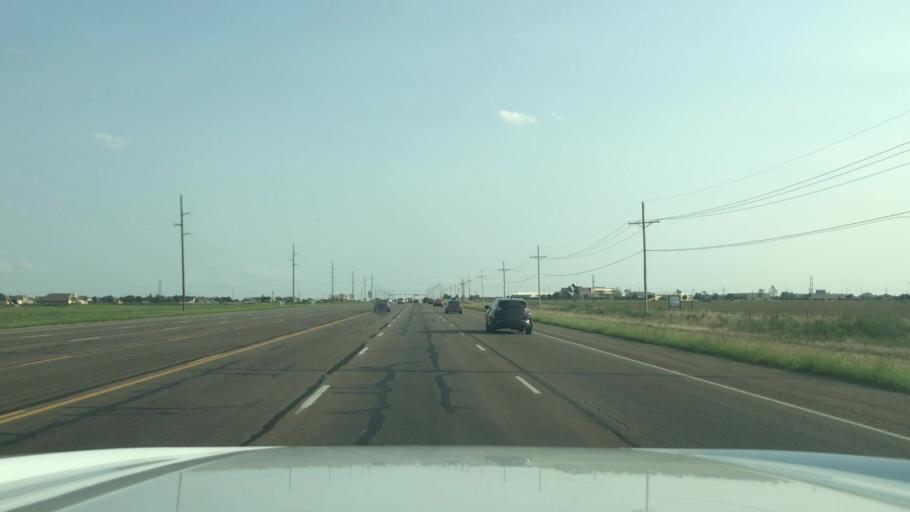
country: US
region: Texas
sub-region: Potter County
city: Amarillo
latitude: 35.1541
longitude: -101.9383
